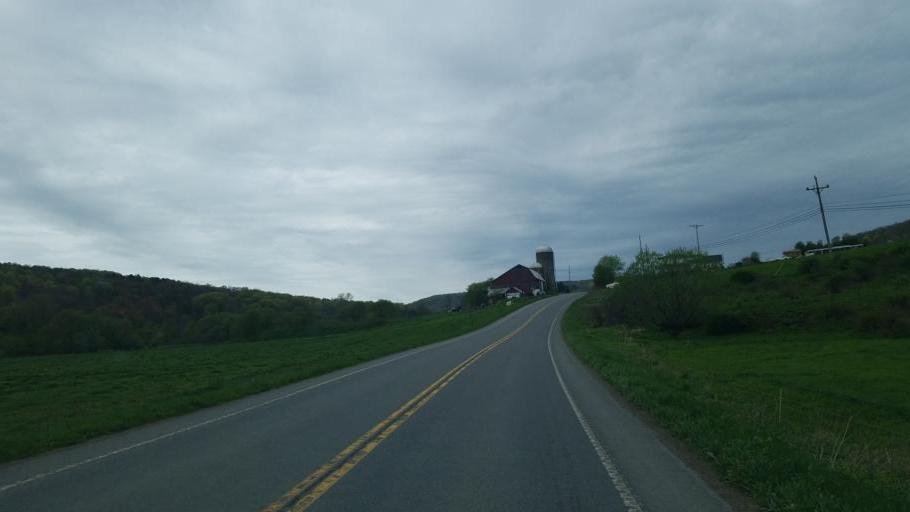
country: US
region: Pennsylvania
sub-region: Tioga County
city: Westfield
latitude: 41.9437
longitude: -77.6692
